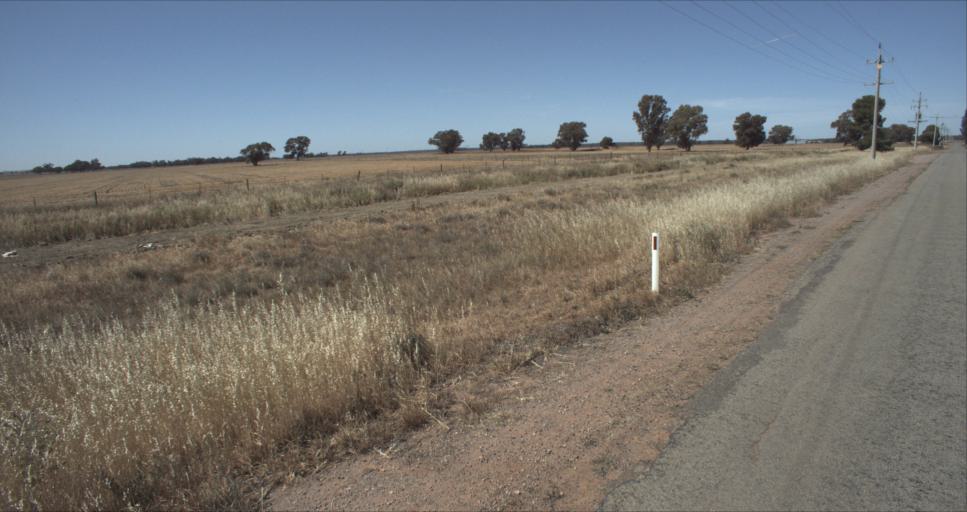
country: AU
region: New South Wales
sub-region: Leeton
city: Leeton
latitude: -34.5708
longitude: 146.3107
